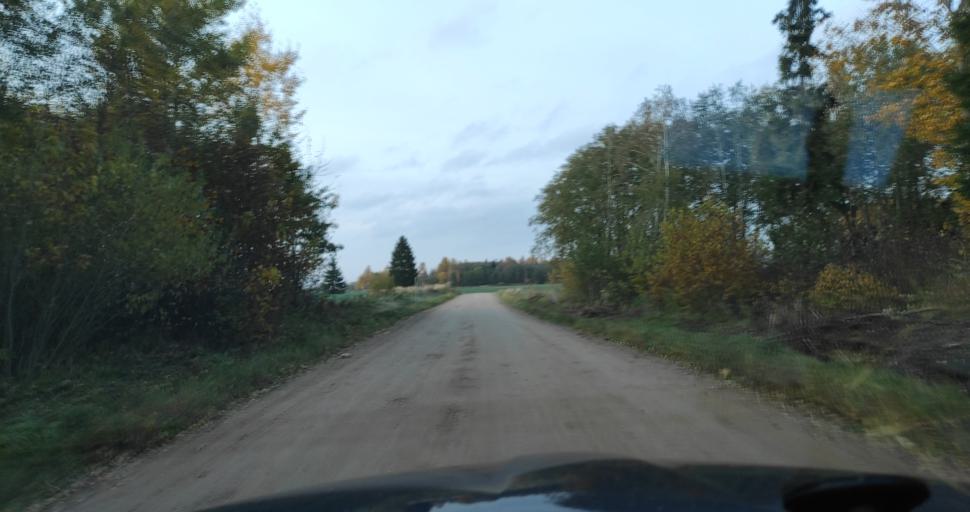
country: LV
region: Skrunda
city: Skrunda
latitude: 56.6359
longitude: 21.8127
